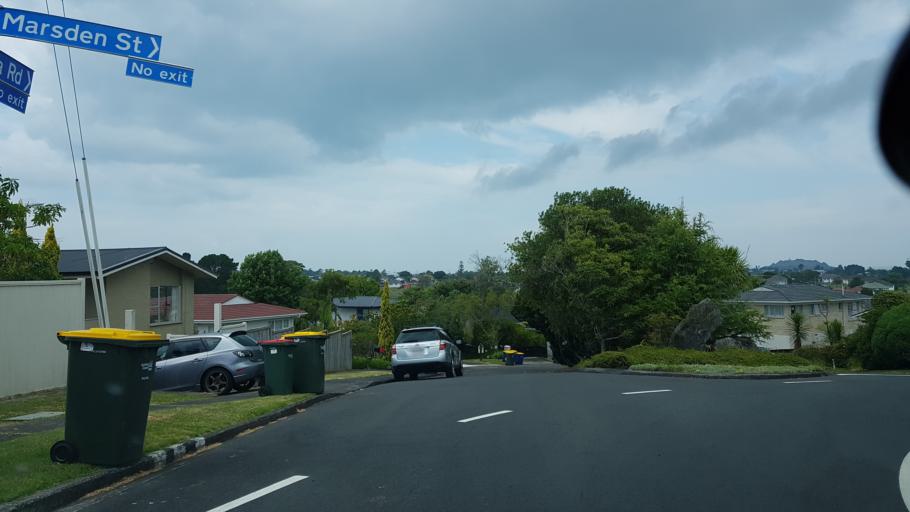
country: NZ
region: Auckland
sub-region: Auckland
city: North Shore
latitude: -36.8037
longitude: 174.7768
